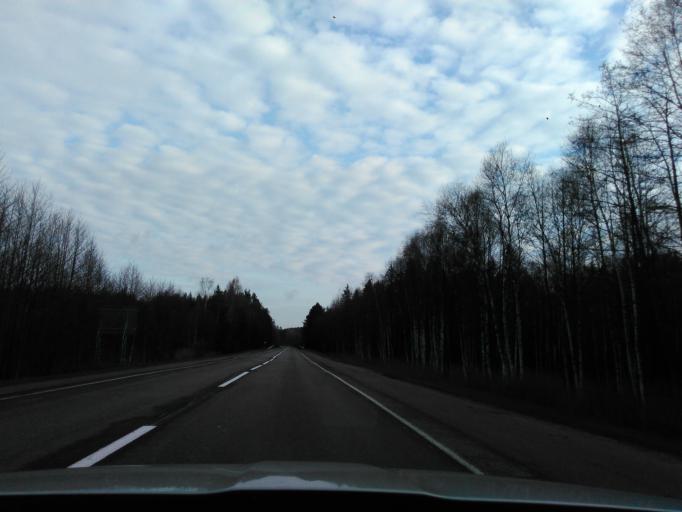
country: BY
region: Minsk
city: Plyeshchanitsy
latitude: 54.3901
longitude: 27.8716
